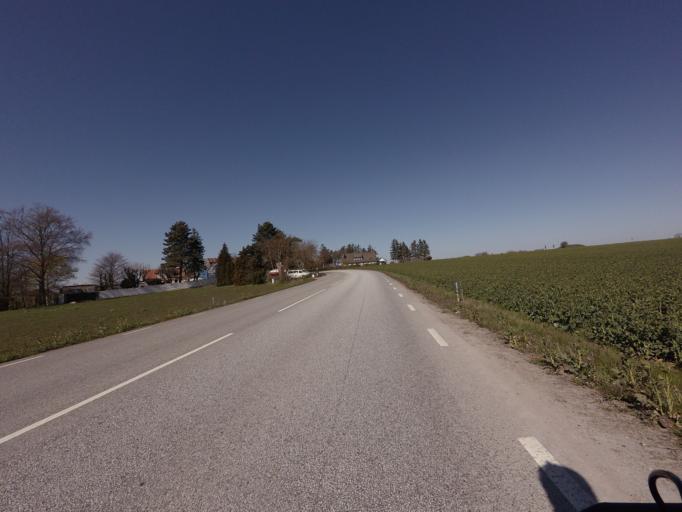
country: SE
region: Skane
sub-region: Vellinge Kommun
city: Vellinge
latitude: 55.4706
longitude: 13.0474
